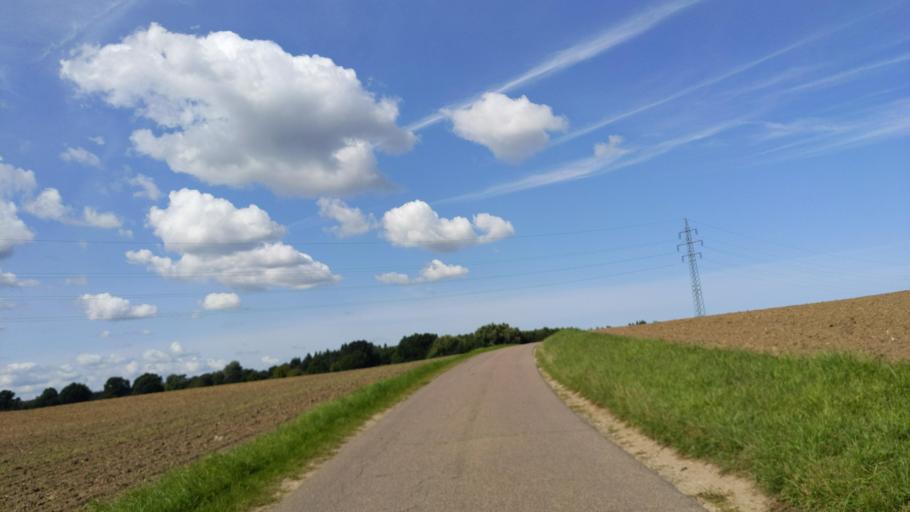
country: DE
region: Schleswig-Holstein
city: Altenkrempe
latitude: 54.1488
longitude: 10.8007
